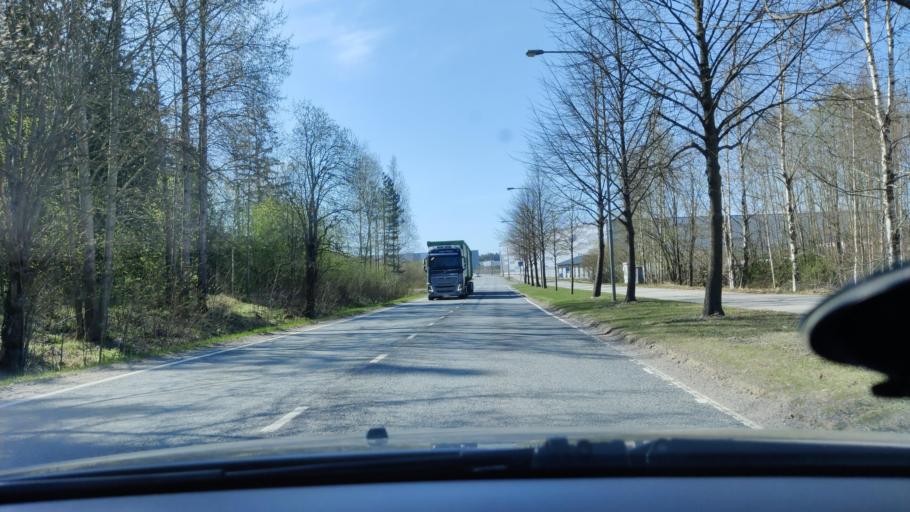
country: FI
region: Uusimaa
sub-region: Helsinki
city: Kerava
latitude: 60.3792
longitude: 25.1060
